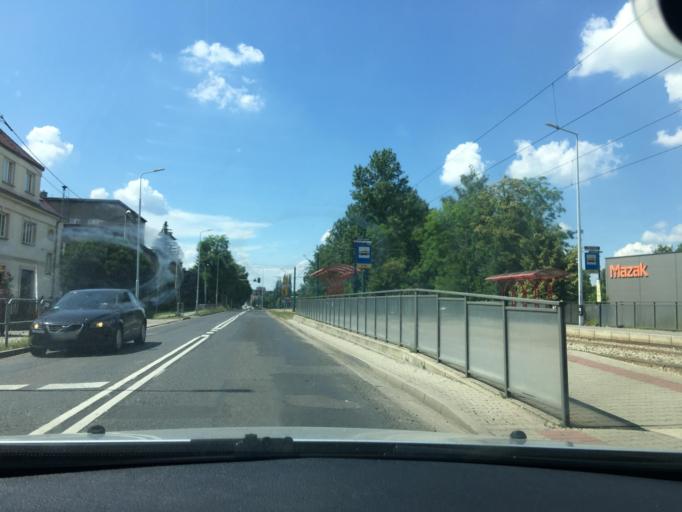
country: PL
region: Silesian Voivodeship
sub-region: Chorzow
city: Chorzow
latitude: 50.2725
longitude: 18.9650
